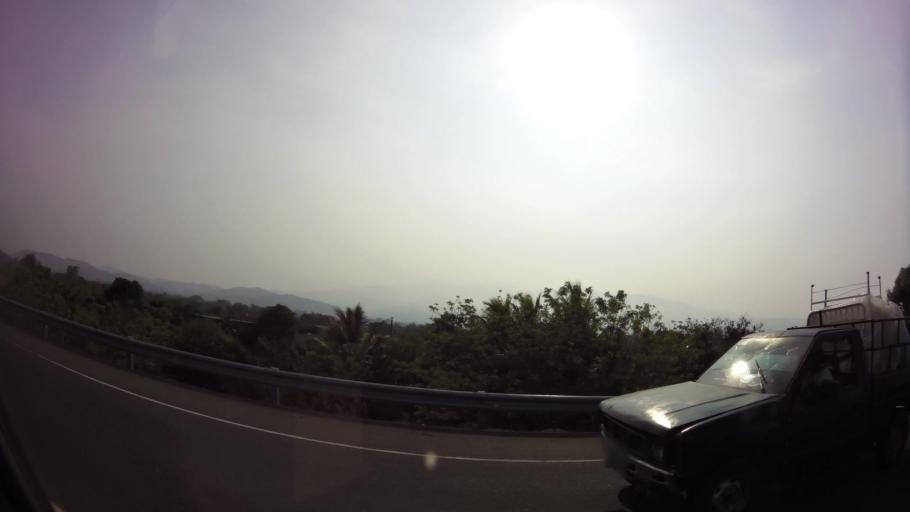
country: HN
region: Comayagua
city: Comayagua
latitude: 14.4420
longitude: -87.6596
